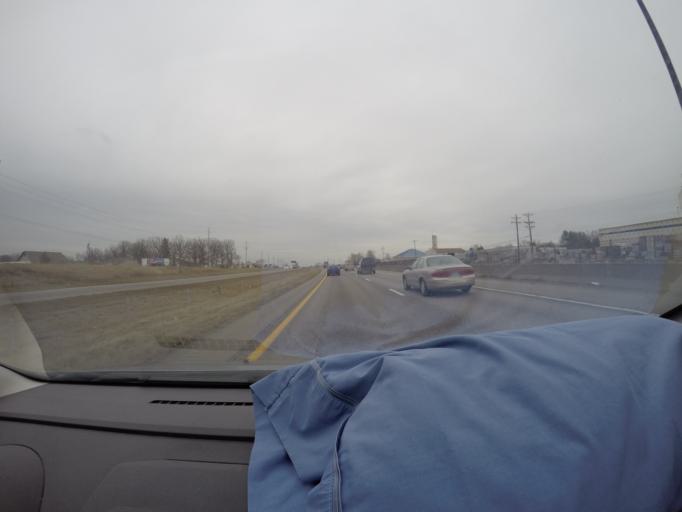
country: US
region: Missouri
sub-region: Saint Charles County
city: Wentzville
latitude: 38.8053
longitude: -90.8890
